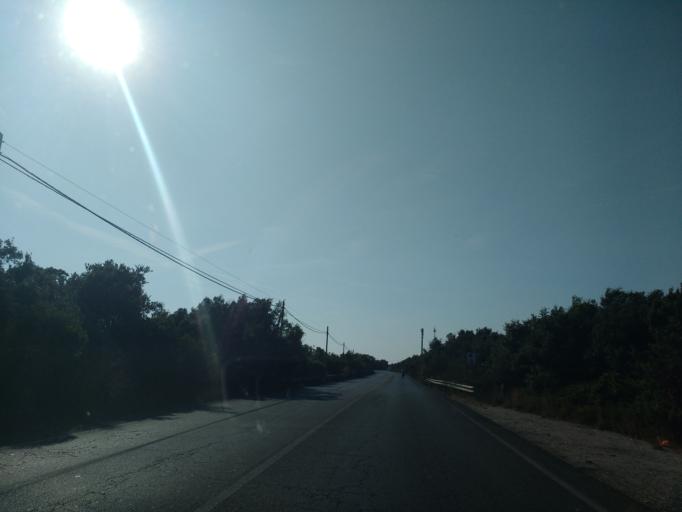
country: IT
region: Latium
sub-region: Citta metropolitana di Roma Capitale
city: Acilia-Castel Fusano-Ostia Antica
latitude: 41.7004
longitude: 12.3519
